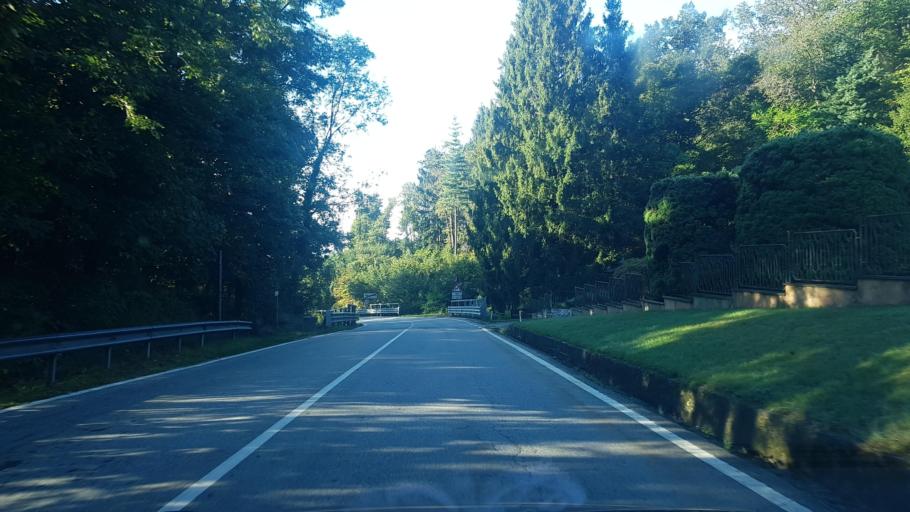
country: IT
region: Piedmont
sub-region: Provincia Verbano-Cusio-Ossola
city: Bee
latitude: 45.9720
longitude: 8.5845
